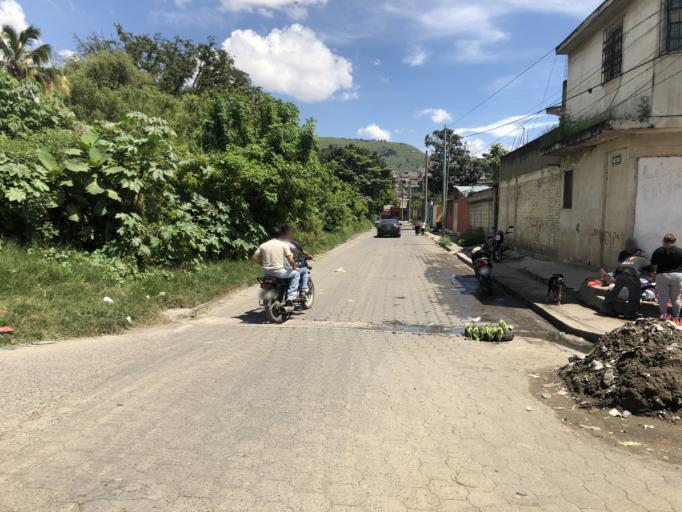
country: GT
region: Guatemala
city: Amatitlan
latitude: 14.4786
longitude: -90.6169
